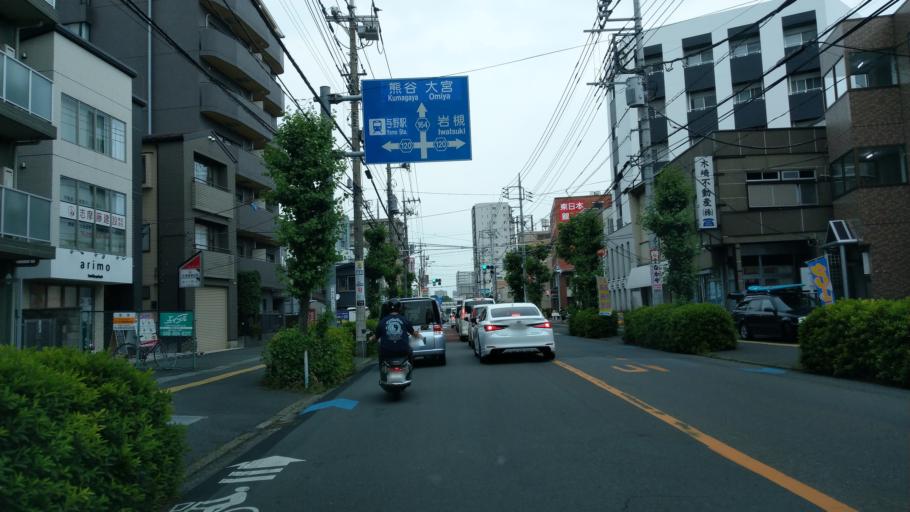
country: JP
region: Saitama
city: Yono
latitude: 35.8848
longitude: 139.6402
